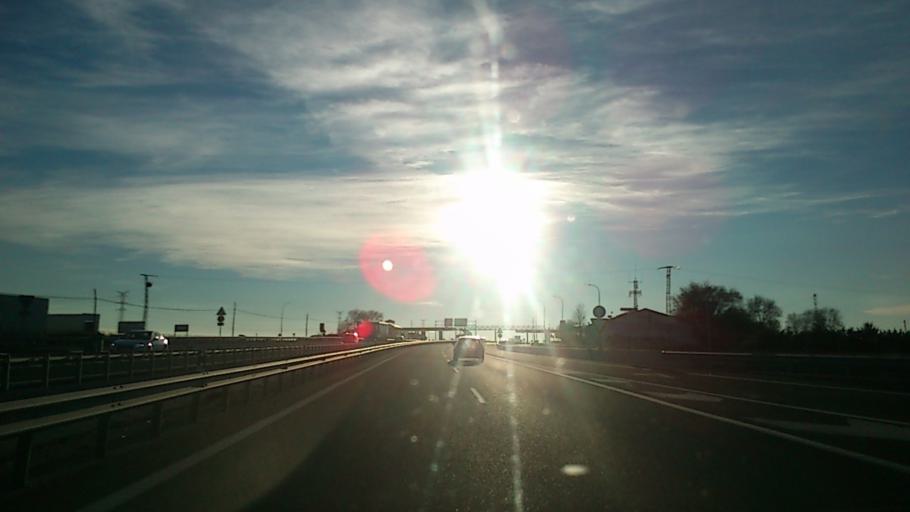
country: ES
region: Castille-La Mancha
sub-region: Provincia de Guadalajara
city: Ledanca
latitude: 40.8620
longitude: -2.8326
